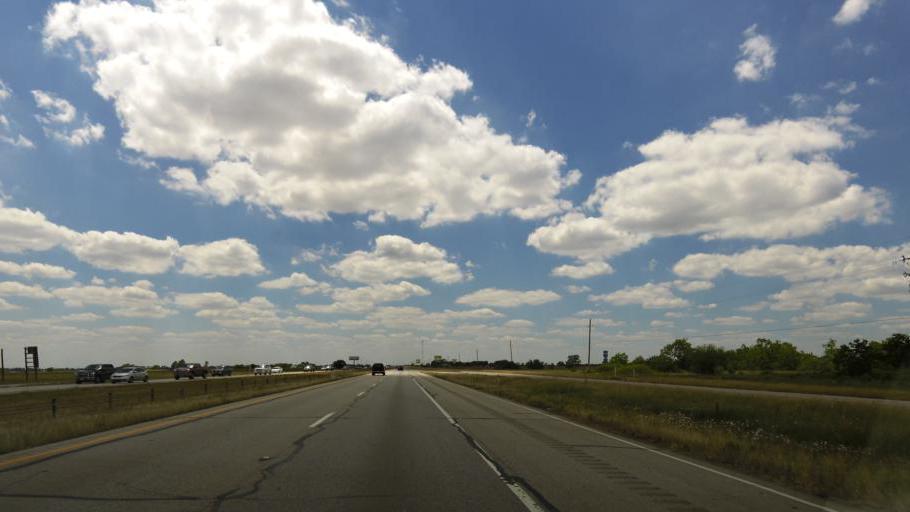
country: US
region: Texas
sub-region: Austin County
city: Sealy
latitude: 29.7522
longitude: -96.2734
